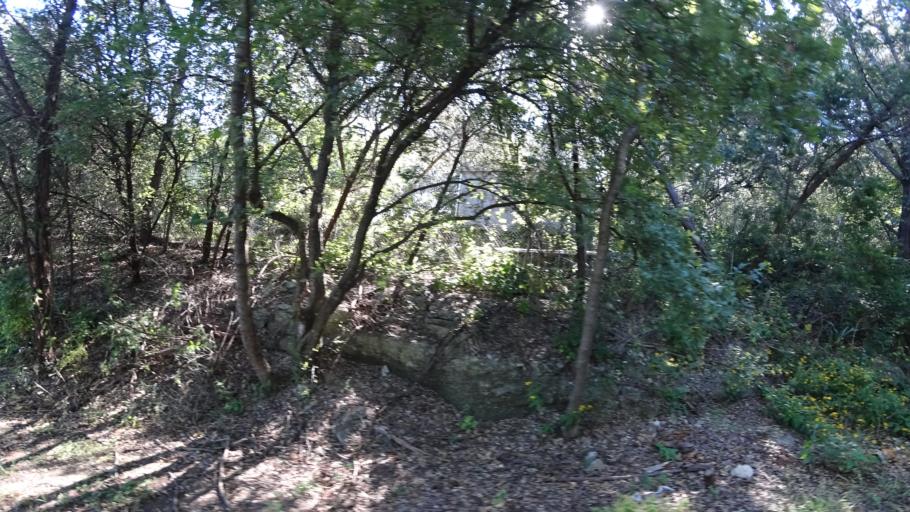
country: US
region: Texas
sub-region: Travis County
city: West Lake Hills
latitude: 30.3303
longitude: -97.7835
